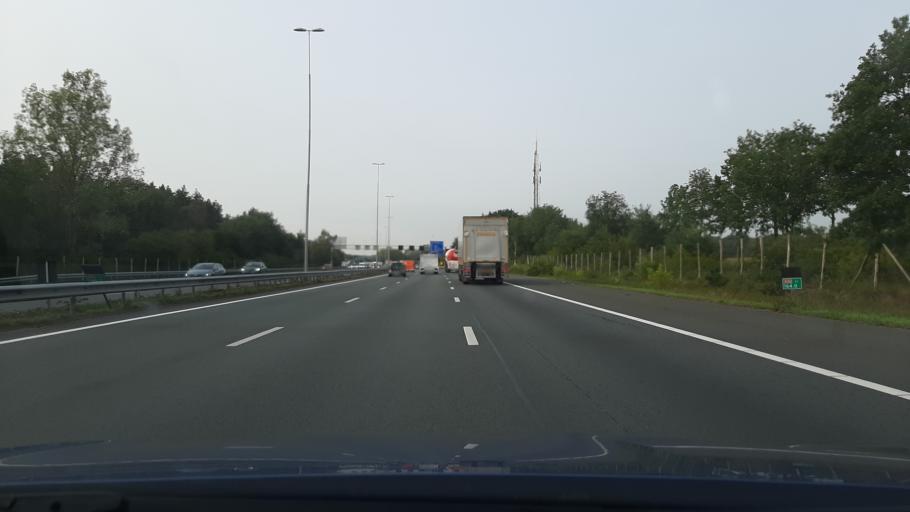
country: NL
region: Gelderland
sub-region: Gemeente Renkum
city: Heelsum
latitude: 51.9866
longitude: 5.7692
